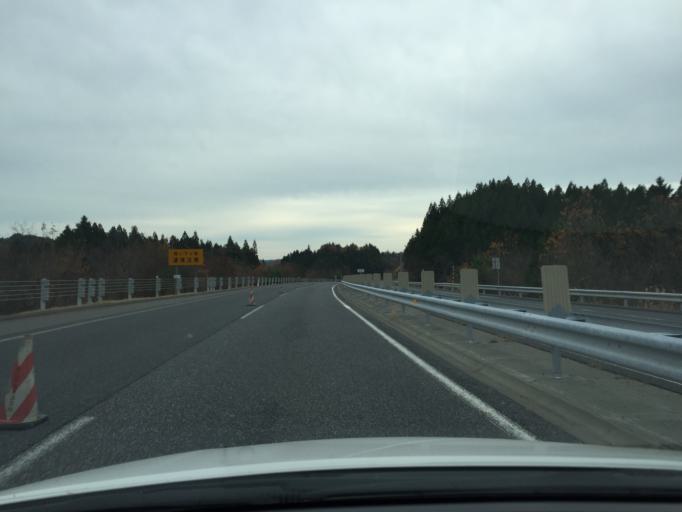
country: JP
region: Fukushima
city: Funehikimachi-funehiki
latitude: 37.2648
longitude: 140.6451
